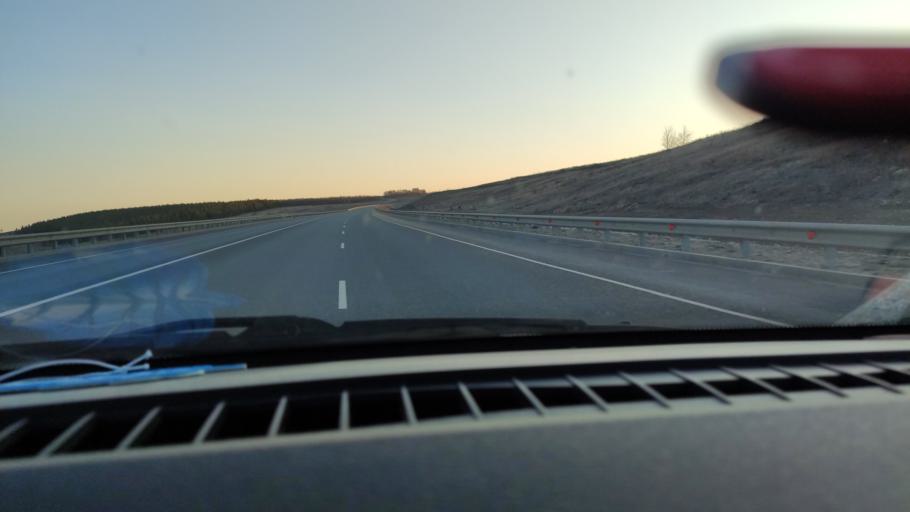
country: RU
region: Saratov
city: Yelshanka
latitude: 51.8748
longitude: 46.5054
